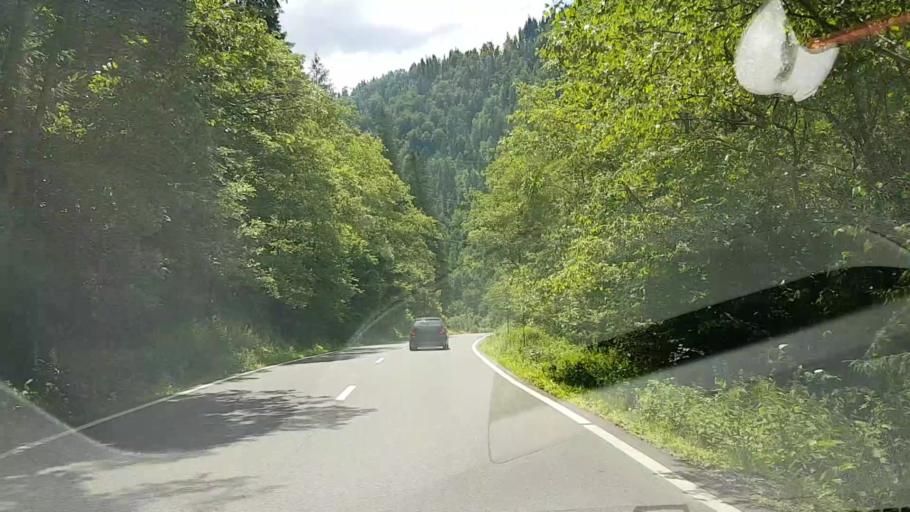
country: RO
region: Suceava
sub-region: Comuna Brosteni
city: Brosteni
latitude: 47.2776
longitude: 25.6495
